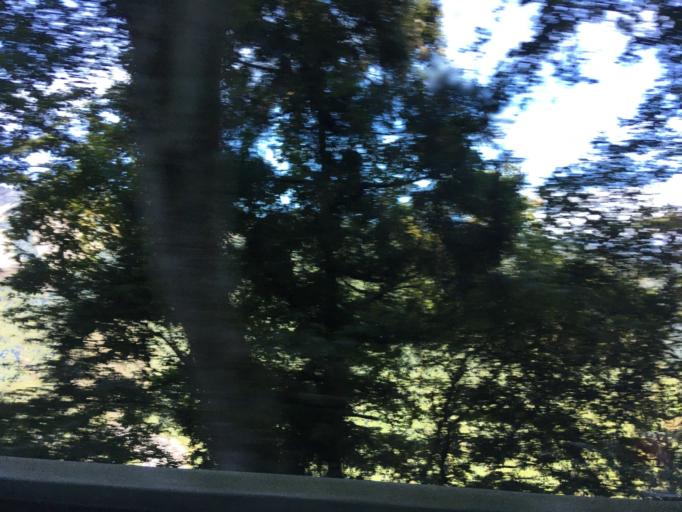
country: TW
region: Taiwan
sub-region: Yilan
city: Yilan
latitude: 24.5482
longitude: 121.5120
